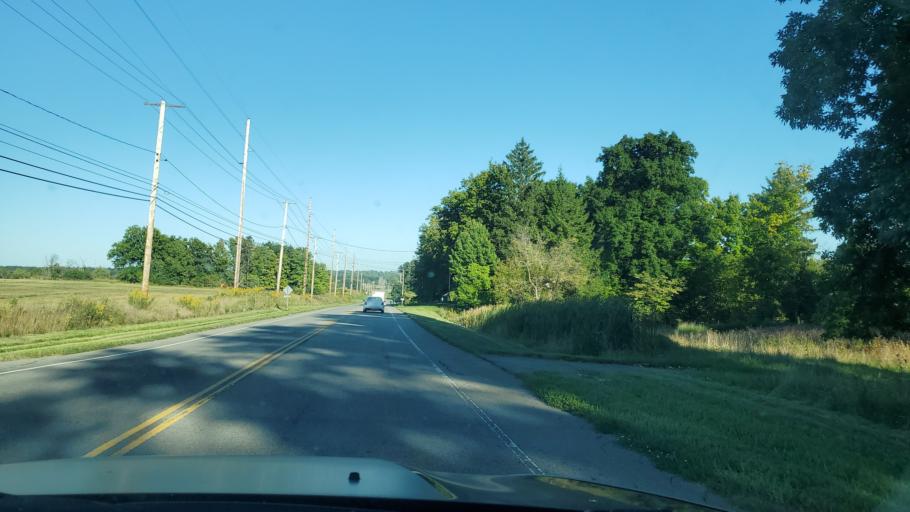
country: US
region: Ohio
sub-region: Mahoning County
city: Boardman
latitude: 40.9881
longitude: -80.7105
